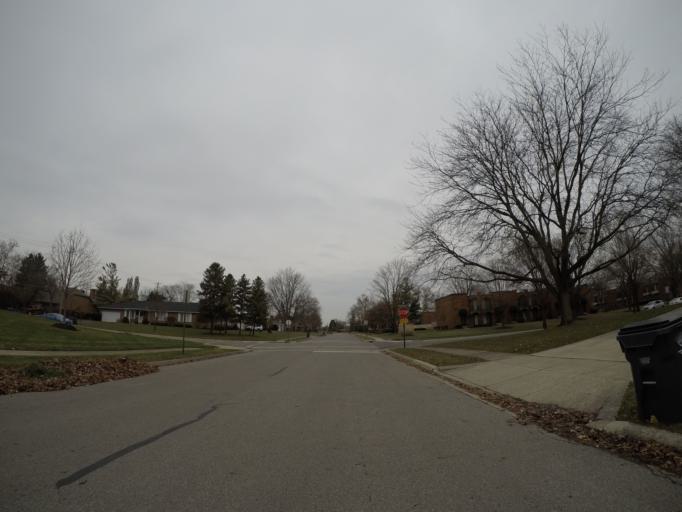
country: US
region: Ohio
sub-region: Franklin County
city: Upper Arlington
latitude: 40.0520
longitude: -83.0742
